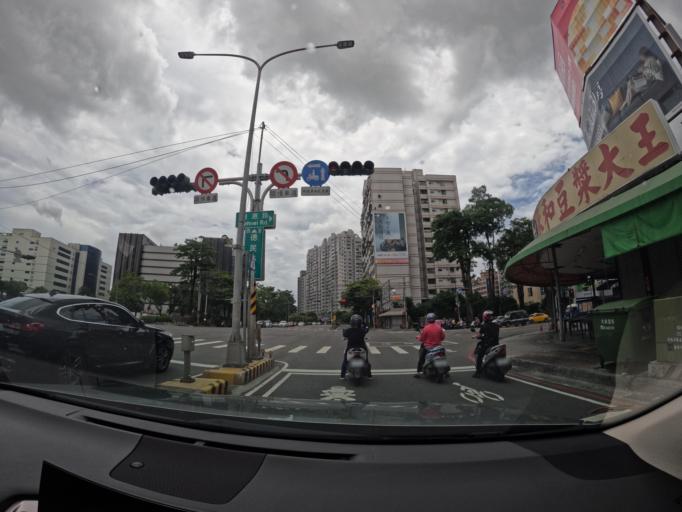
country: TW
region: Kaohsiung
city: Kaohsiung
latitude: 22.7255
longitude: 120.3032
